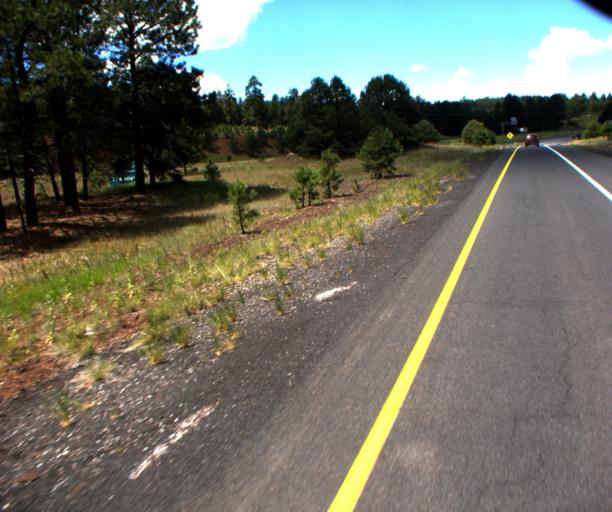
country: US
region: Arizona
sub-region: Coconino County
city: Flagstaff
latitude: 35.1928
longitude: -111.7292
